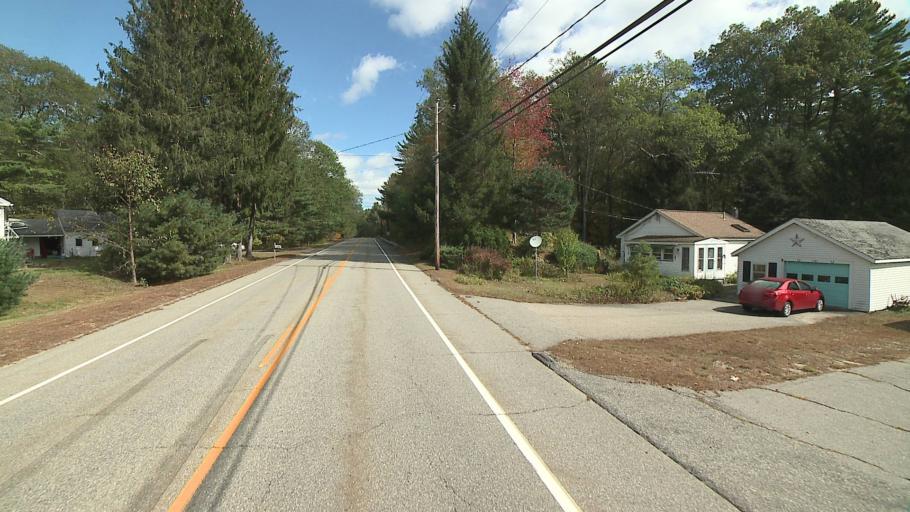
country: US
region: Connecticut
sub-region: Windham County
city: North Grosvenor Dale
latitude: 42.0046
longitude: -71.8971
